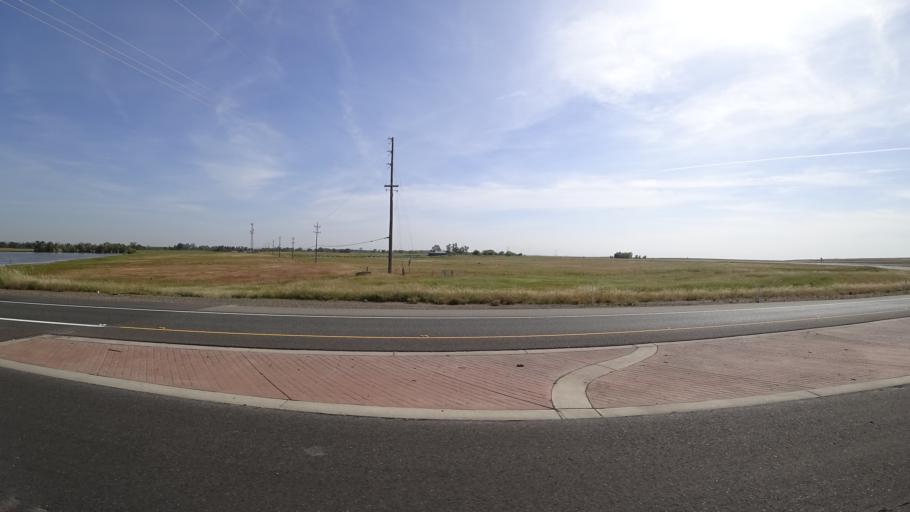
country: US
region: California
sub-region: Butte County
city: Durham
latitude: 39.6182
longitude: -121.6869
